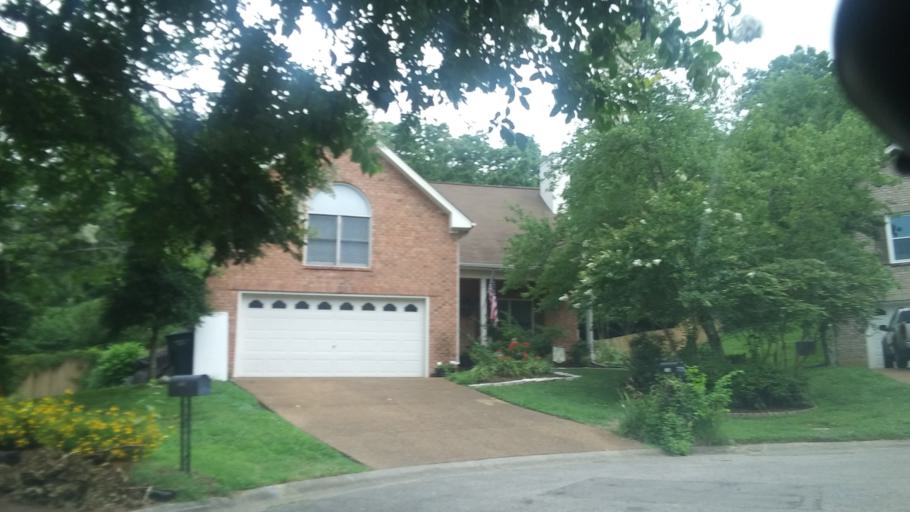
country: US
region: Tennessee
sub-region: Davidson County
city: Belle Meade
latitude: 36.0869
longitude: -86.9348
